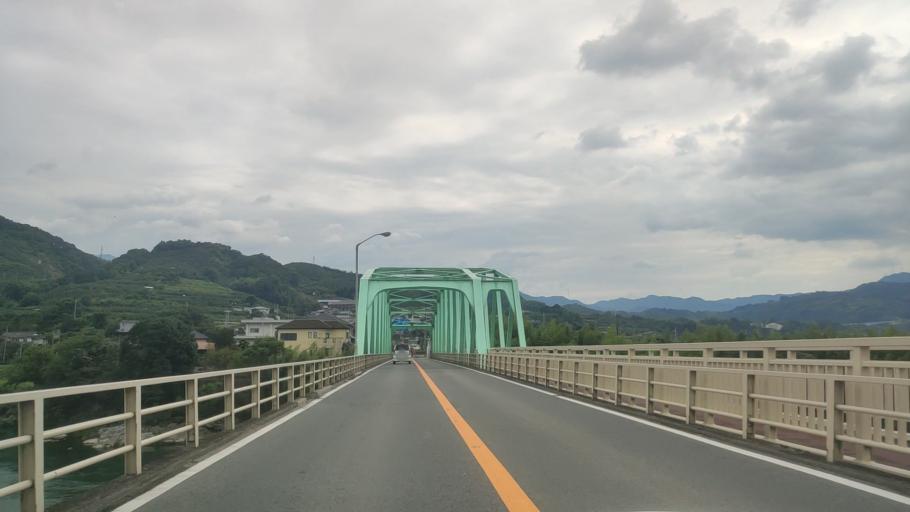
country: JP
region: Wakayama
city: Hashimoto
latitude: 34.2990
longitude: 135.5783
